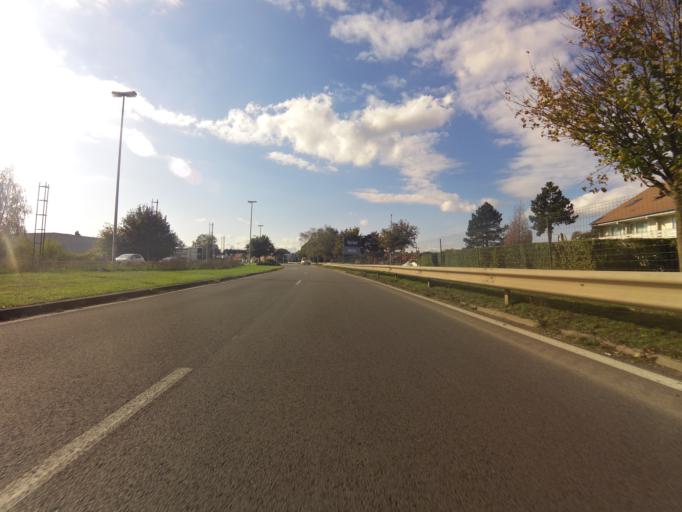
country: FR
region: Nord-Pas-de-Calais
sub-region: Departement du Nord
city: Proville
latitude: 50.1762
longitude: 3.2072
